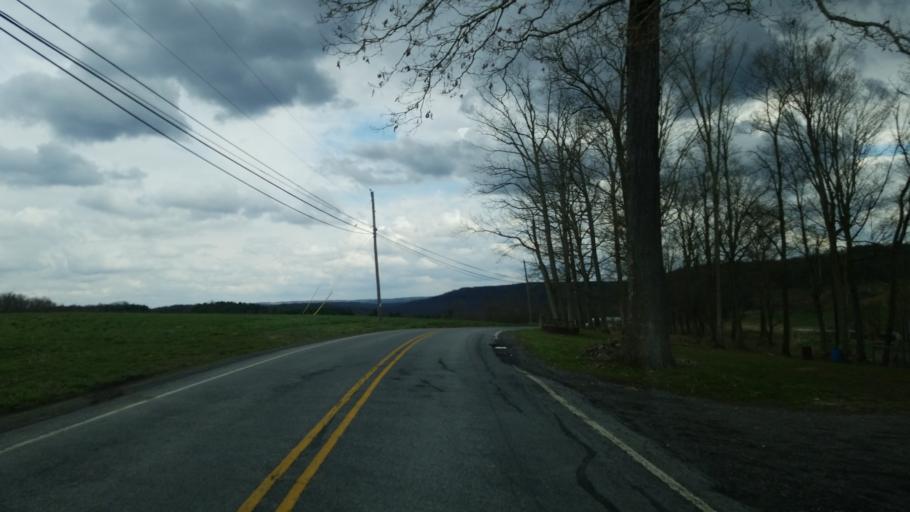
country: US
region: Pennsylvania
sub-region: Clearfield County
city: Curwensville
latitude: 40.8961
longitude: -78.4819
